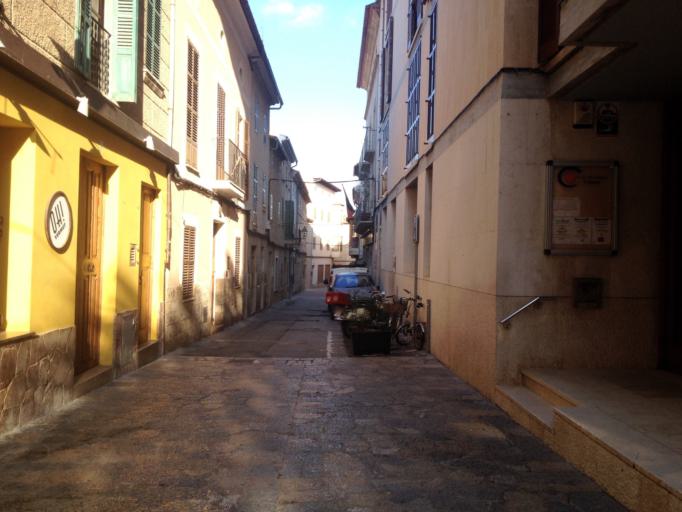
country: ES
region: Balearic Islands
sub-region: Illes Balears
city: Pollenca
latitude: 39.8773
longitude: 3.0165
